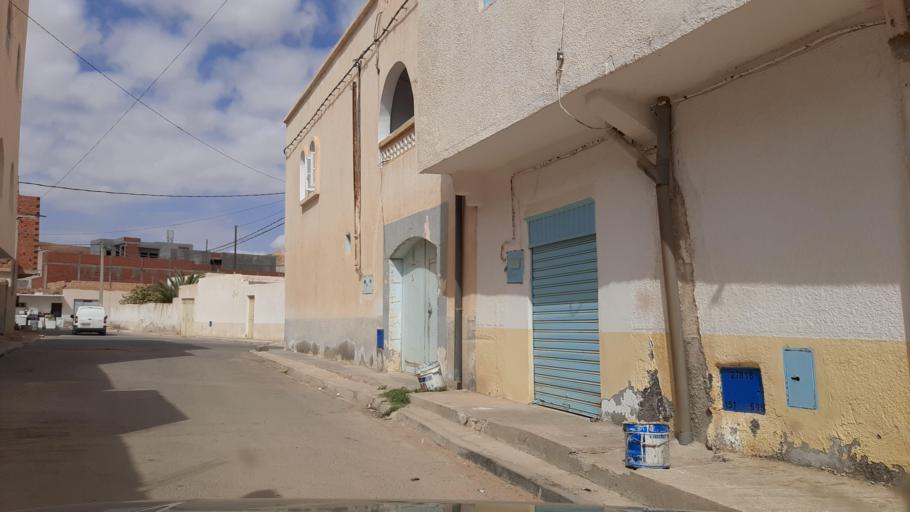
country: TN
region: Tataouine
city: Tataouine
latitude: 32.9319
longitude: 10.4549
